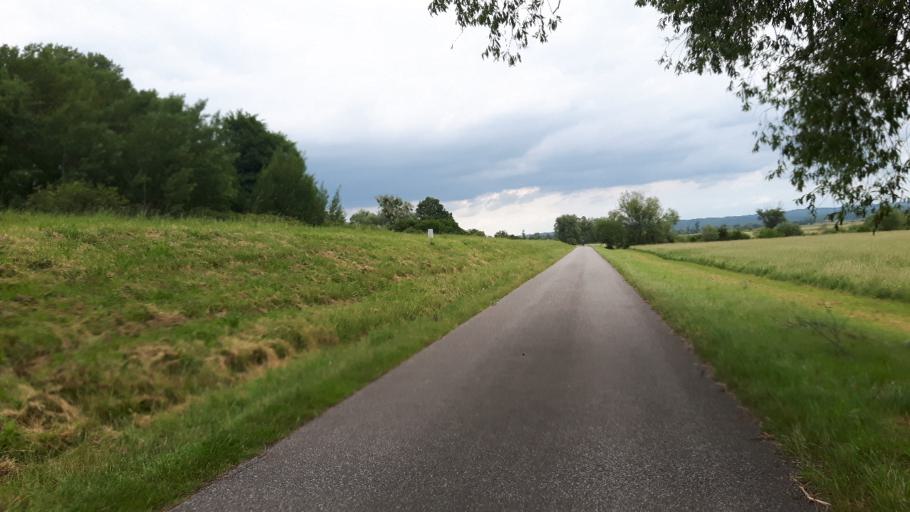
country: DE
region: Brandenburg
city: Schoneberg
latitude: 52.9867
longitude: 14.1529
